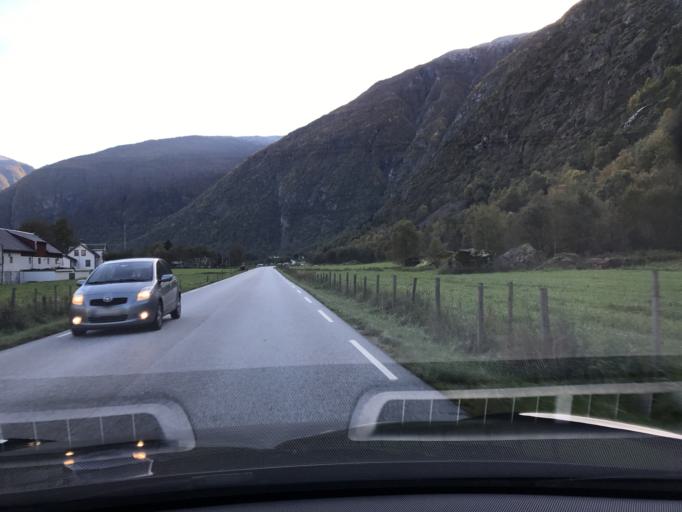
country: NO
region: Sogn og Fjordane
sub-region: Laerdal
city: Laerdalsoyri
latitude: 61.0870
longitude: 7.5118
